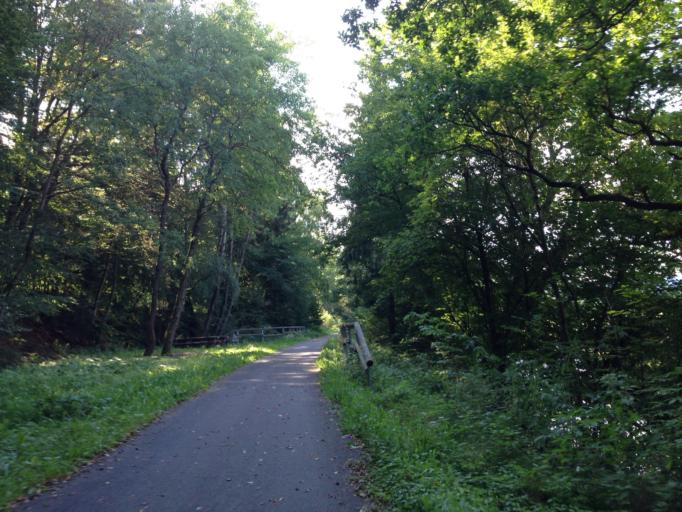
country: DE
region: Hesse
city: Hatzfeld
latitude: 50.9901
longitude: 8.5181
